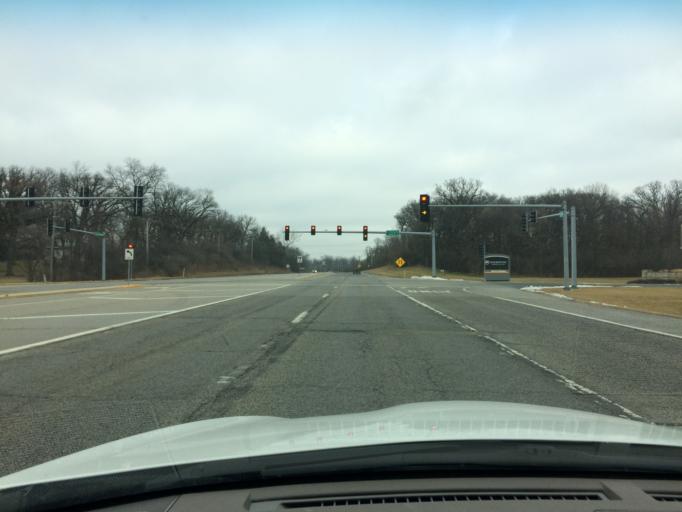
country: US
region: Illinois
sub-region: Kane County
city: Sugar Grove
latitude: 41.8004
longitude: -88.4614
